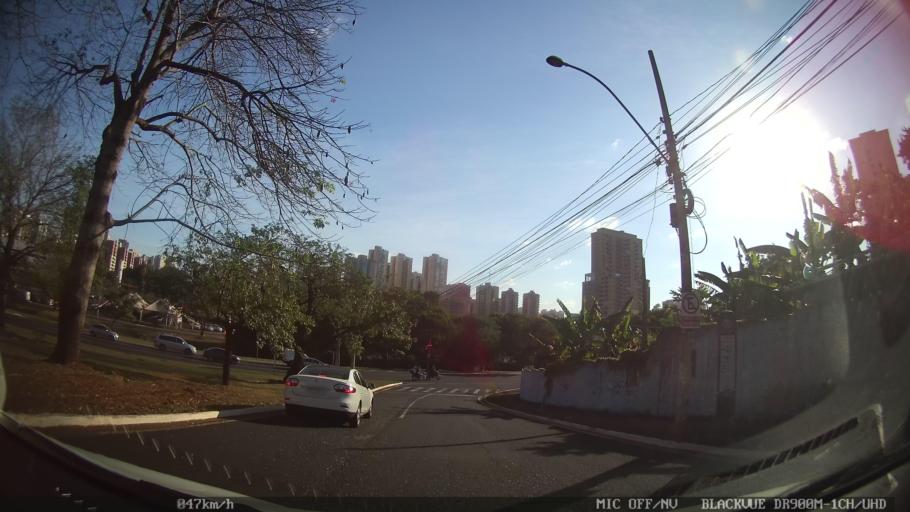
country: BR
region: Sao Paulo
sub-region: Ribeirao Preto
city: Ribeirao Preto
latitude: -21.2069
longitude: -47.7896
